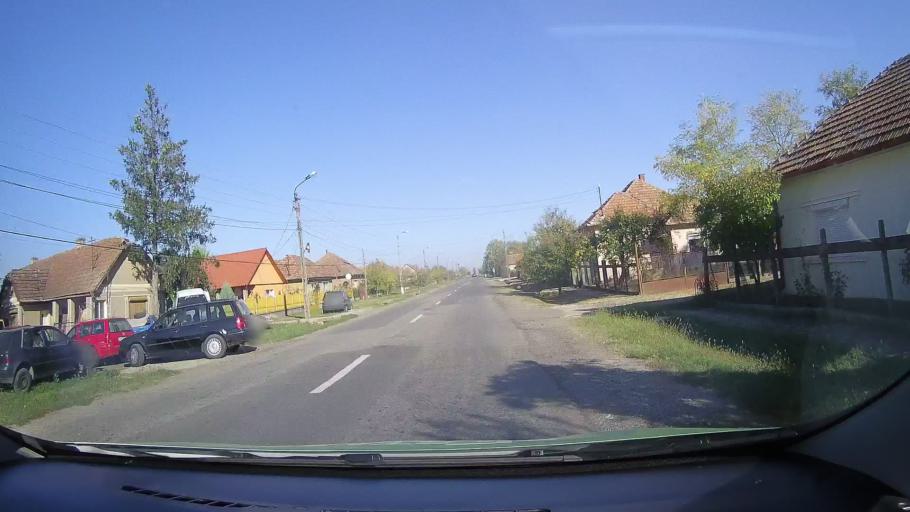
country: RO
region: Satu Mare
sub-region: Oras Tasnad
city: Tasnad
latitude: 47.5087
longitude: 22.5733
